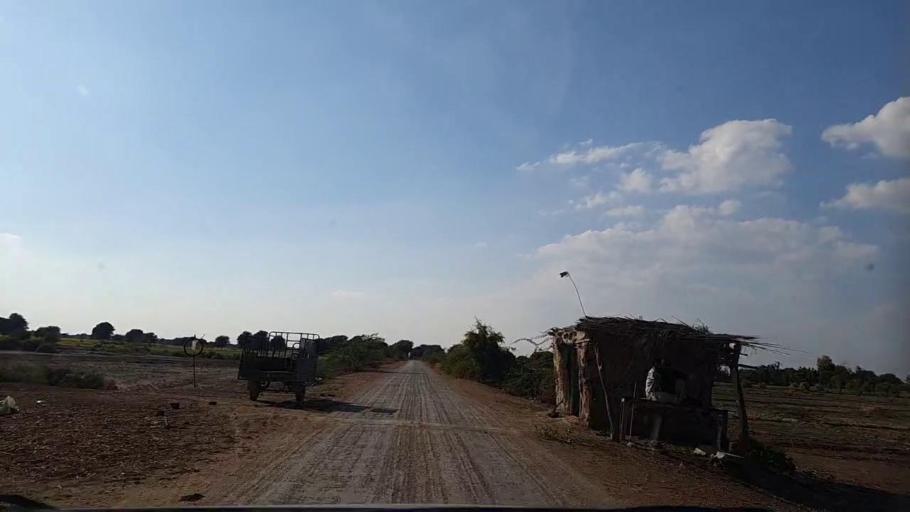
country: PK
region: Sindh
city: Pithoro
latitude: 25.6498
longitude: 69.2889
